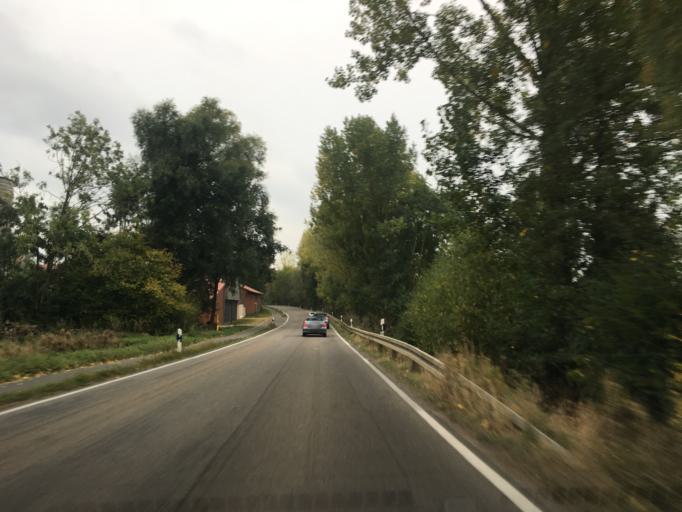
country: DE
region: North Rhine-Westphalia
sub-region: Regierungsbezirk Munster
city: Nordwalde
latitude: 52.0679
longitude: 7.4809
